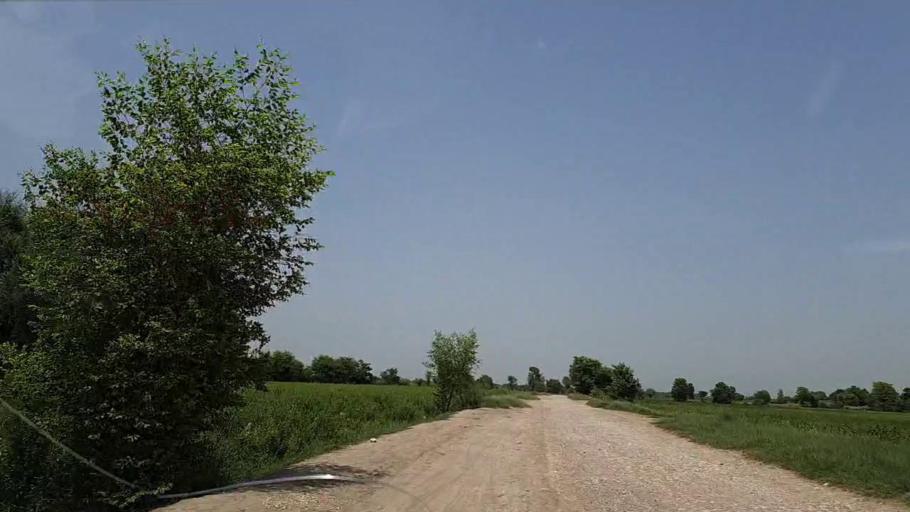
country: PK
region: Sindh
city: Tharu Shah
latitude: 26.9527
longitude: 68.0434
